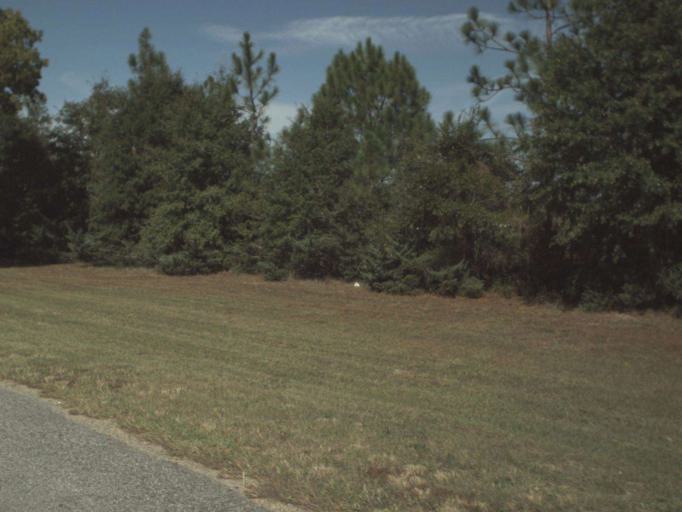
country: US
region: Florida
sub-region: Okaloosa County
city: Crestview
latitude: 30.7224
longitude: -86.6835
